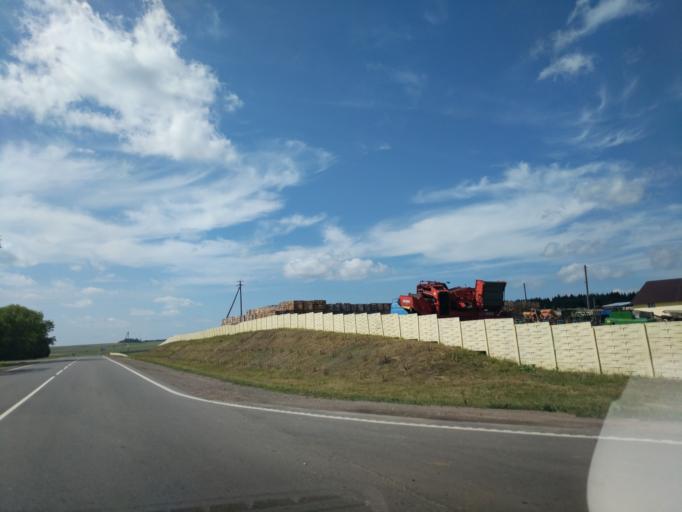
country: BY
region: Minsk
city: Syomkava
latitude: 54.1097
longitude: 27.4566
